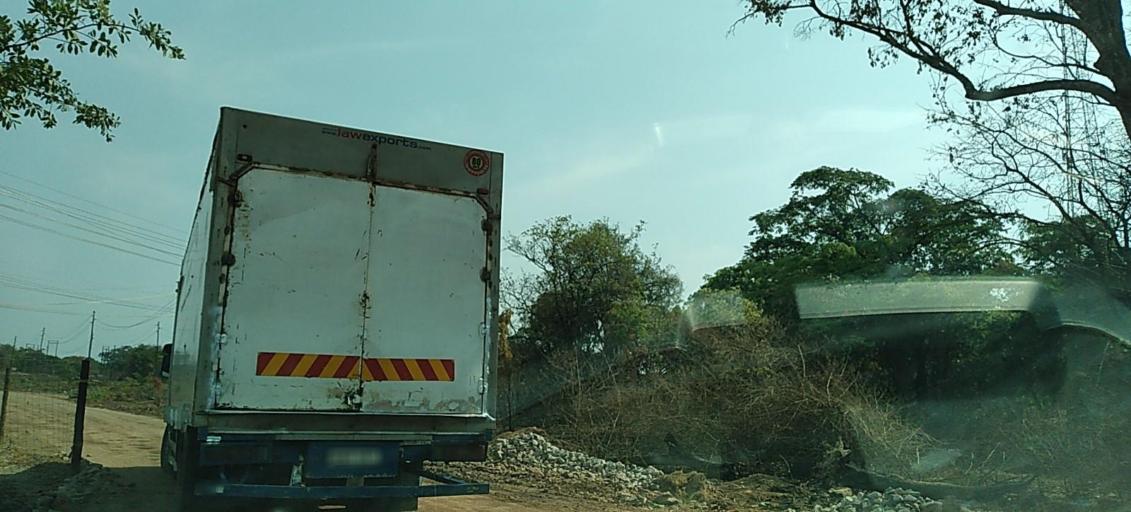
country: ZM
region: Copperbelt
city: Chililabombwe
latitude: -12.2983
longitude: 27.7734
